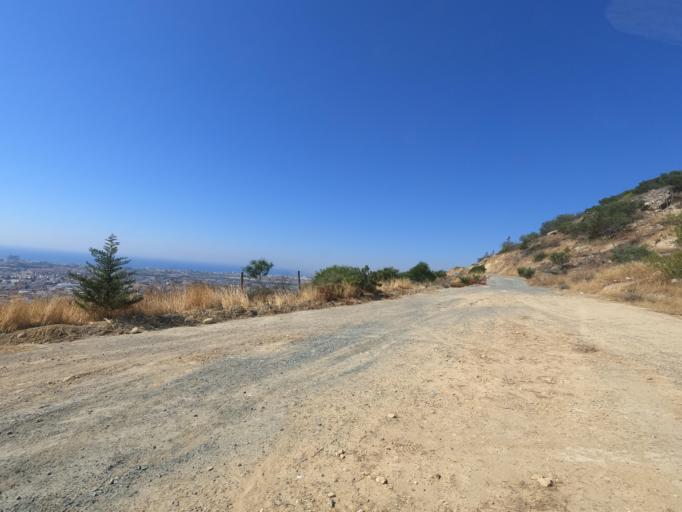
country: CY
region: Larnaka
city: Voroklini
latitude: 34.9916
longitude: 33.6515
